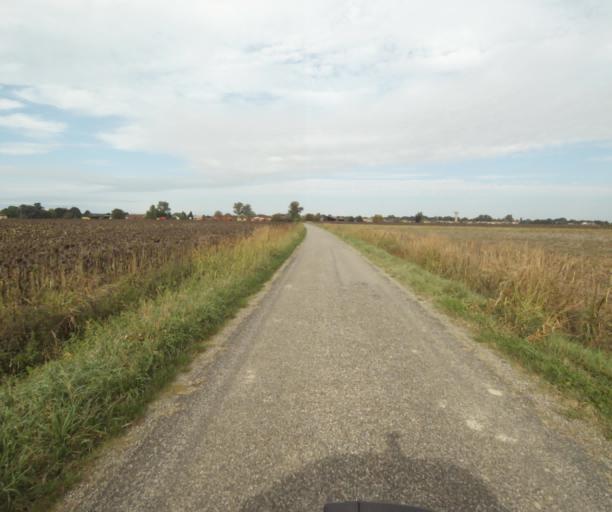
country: FR
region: Midi-Pyrenees
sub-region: Departement du Tarn-et-Garonne
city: Finhan
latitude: 43.9054
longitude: 1.2337
